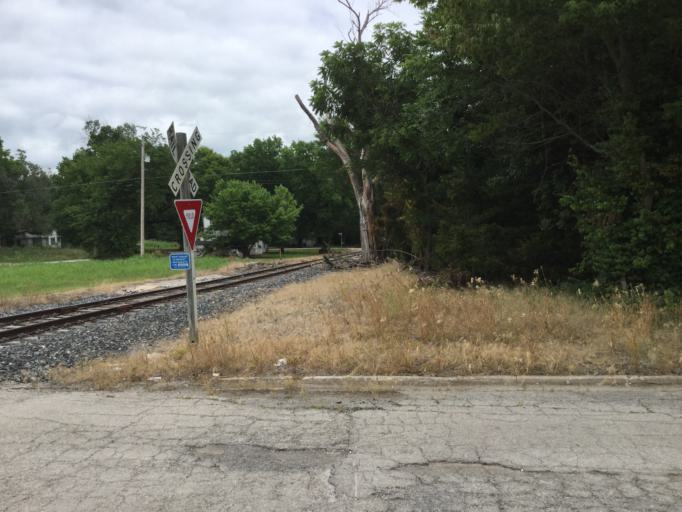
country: US
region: Kansas
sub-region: Montgomery County
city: Independence
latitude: 37.2174
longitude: -95.7188
